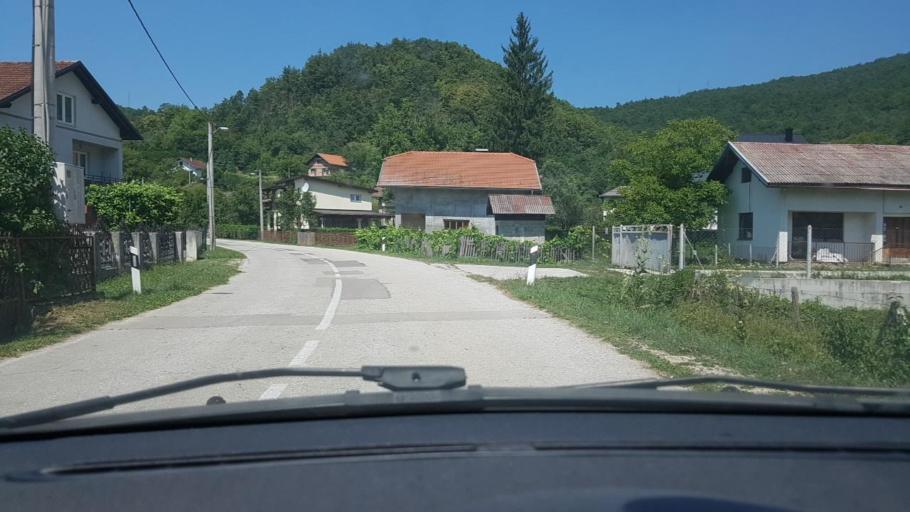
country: BA
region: Federation of Bosnia and Herzegovina
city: Orasac
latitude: 44.5674
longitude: 16.0993
